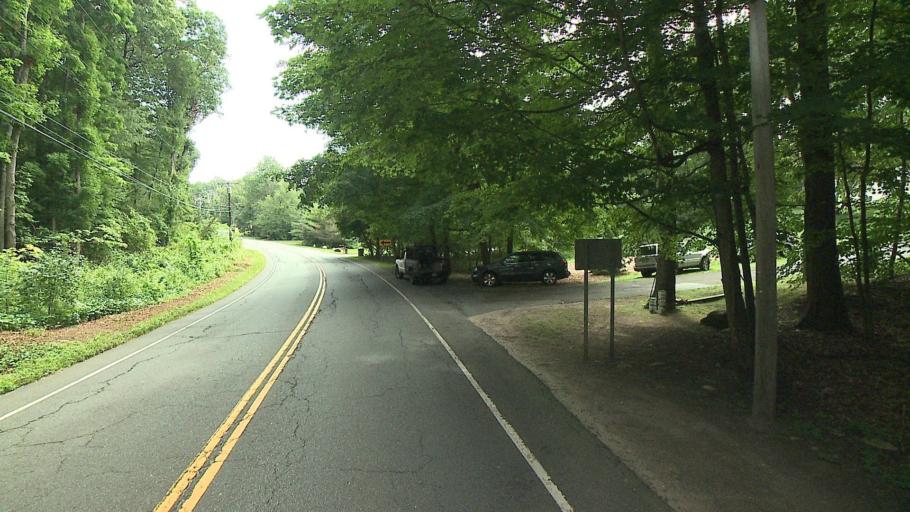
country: US
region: New York
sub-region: Putnam County
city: Putnam Lake
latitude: 41.4447
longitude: -73.5227
